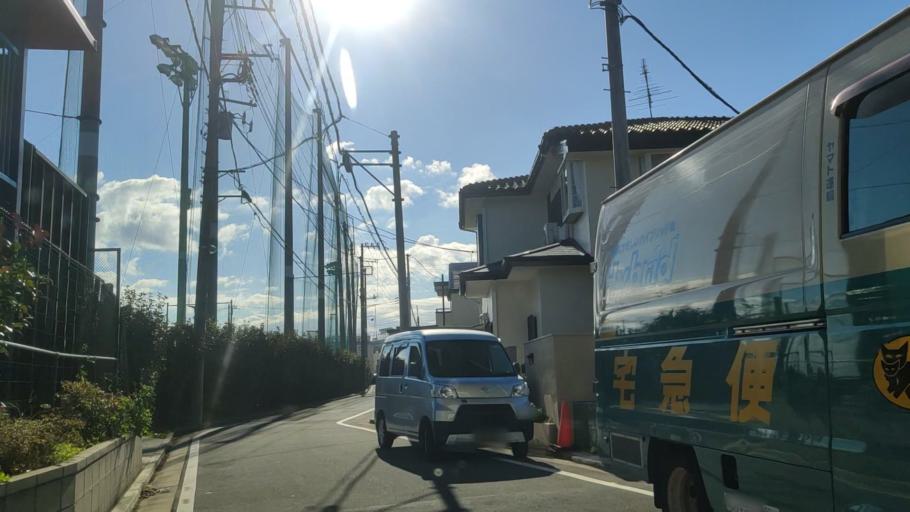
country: JP
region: Kanagawa
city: Yokohama
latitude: 35.4232
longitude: 139.6485
